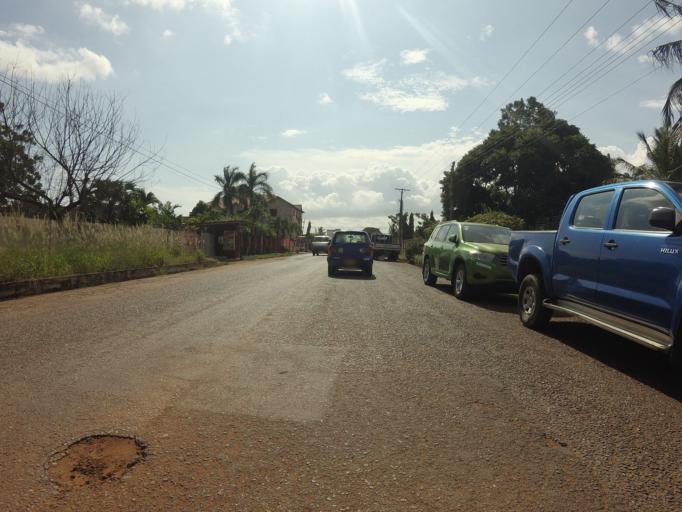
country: GH
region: Greater Accra
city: Medina Estates
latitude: 5.6688
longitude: -0.1849
